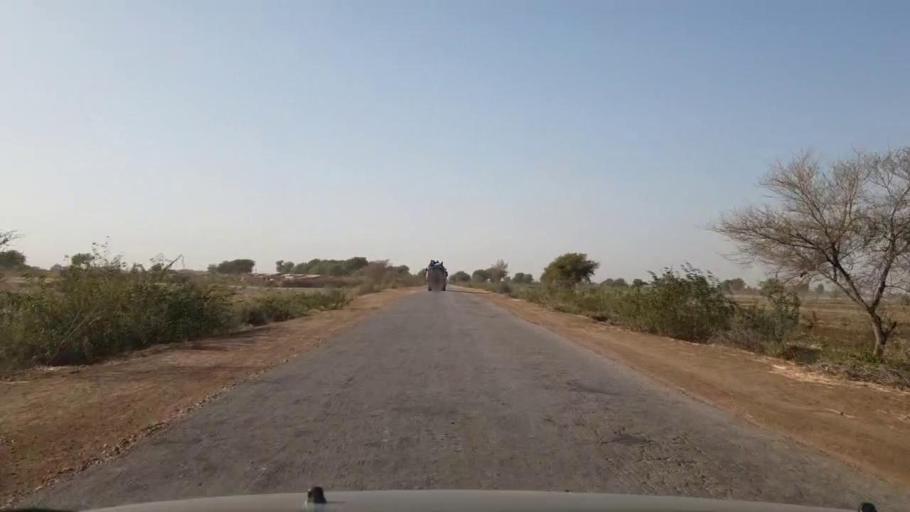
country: PK
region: Sindh
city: Tando Ghulam Ali
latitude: 25.1839
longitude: 68.8179
